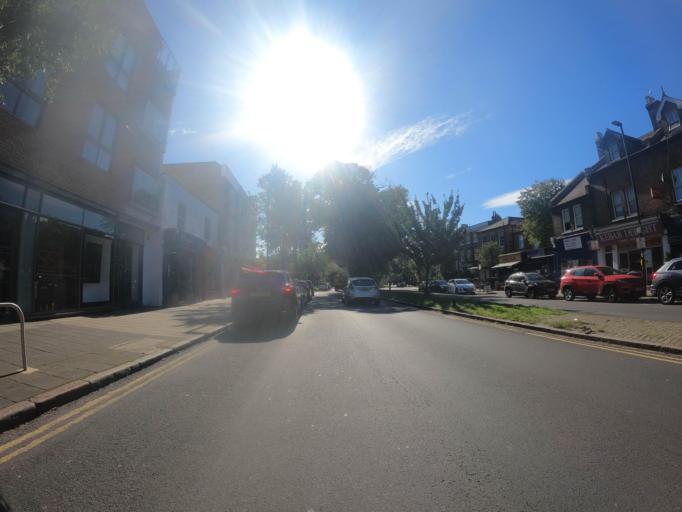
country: GB
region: England
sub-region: Greater London
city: Ealing
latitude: 51.5062
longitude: -0.3051
